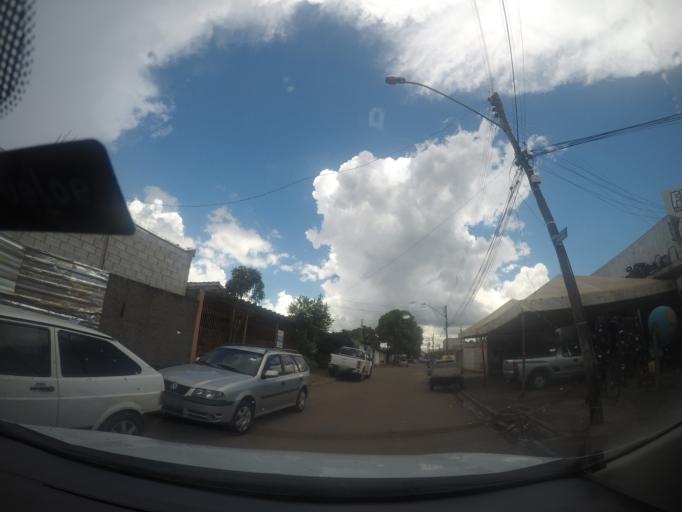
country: BR
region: Goias
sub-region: Goiania
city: Goiania
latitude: -16.6930
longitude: -49.3151
